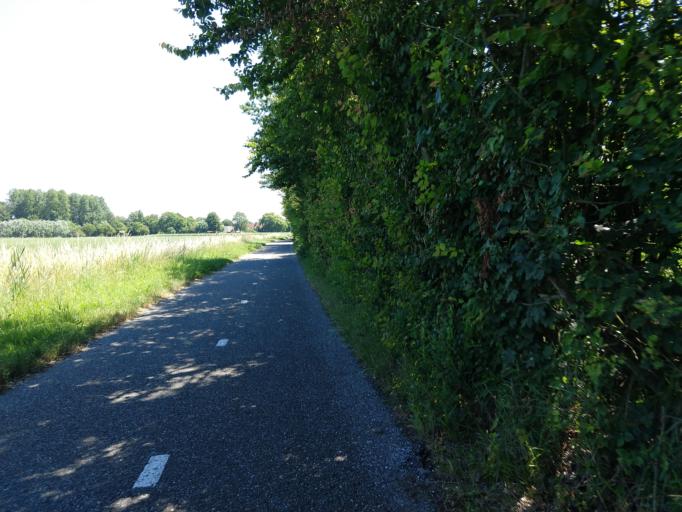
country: NL
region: Zeeland
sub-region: Gemeente Veere
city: Veere
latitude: 51.5434
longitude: 3.6539
